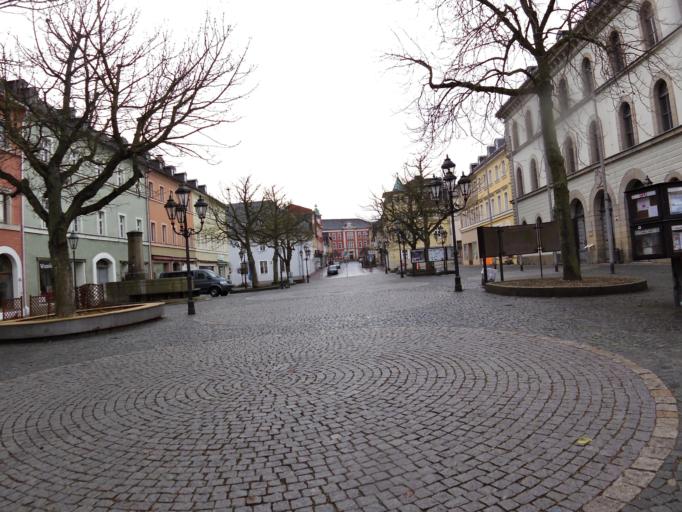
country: DE
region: Bavaria
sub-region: Upper Franconia
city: Wunsiedel
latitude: 50.0376
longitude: 12.0028
